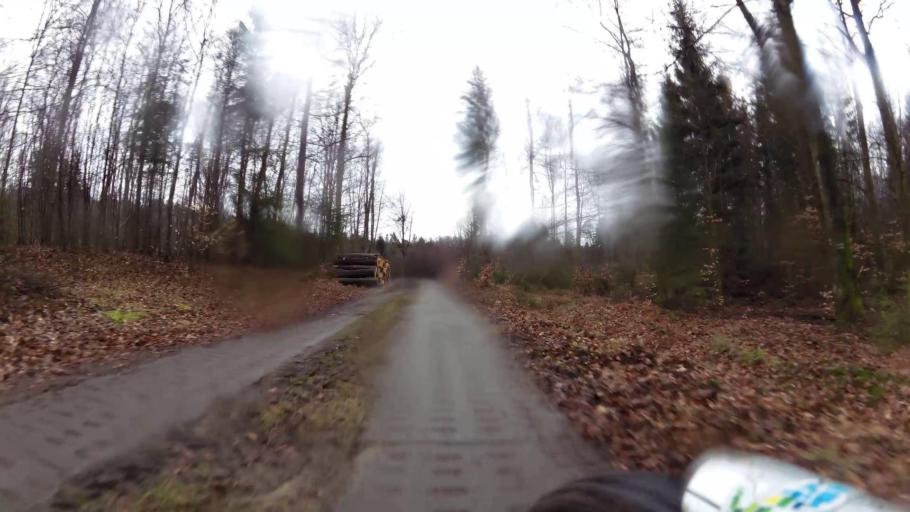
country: PL
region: Pomeranian Voivodeship
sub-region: Powiat bytowski
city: Miastko
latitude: 54.0350
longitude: 17.0253
